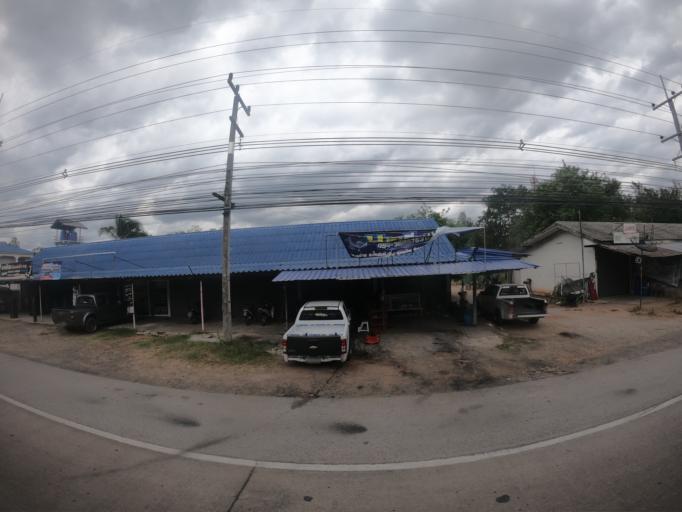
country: TH
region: Nakhon Ratchasima
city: Nakhon Ratchasima
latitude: 14.8885
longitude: 102.1682
